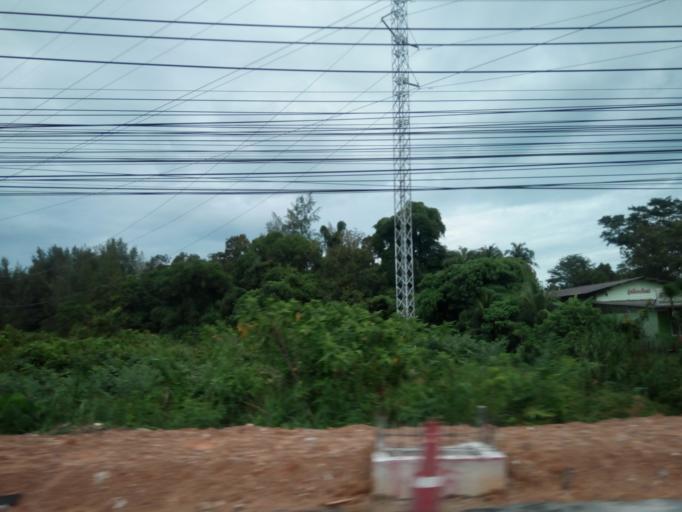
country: TH
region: Phuket
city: Thalang
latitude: 8.0980
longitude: 98.3364
